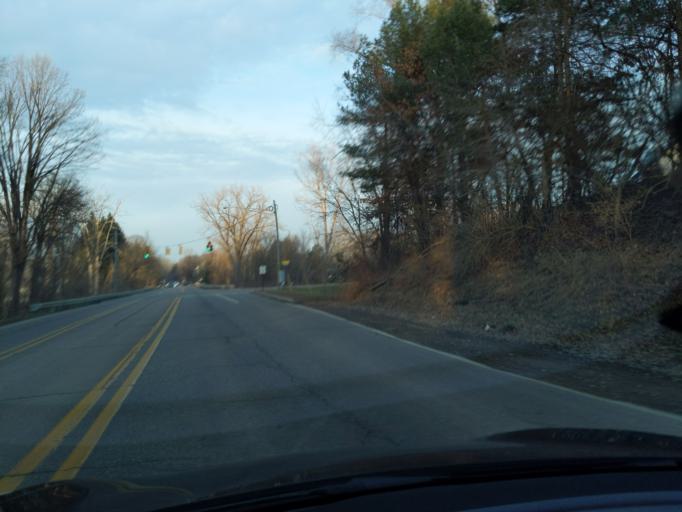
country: US
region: Michigan
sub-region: Livingston County
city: Brighton
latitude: 42.5993
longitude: -83.7514
